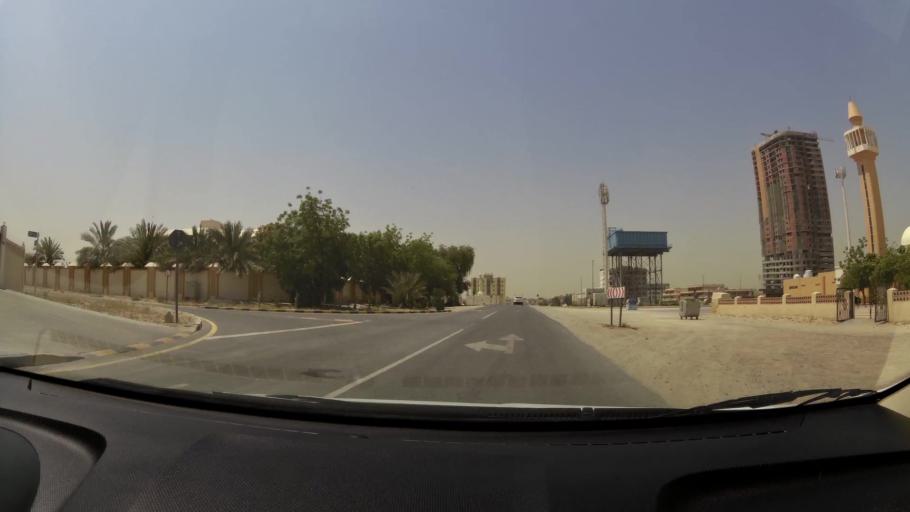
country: AE
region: Ajman
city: Ajman
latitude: 25.4003
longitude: 55.5138
